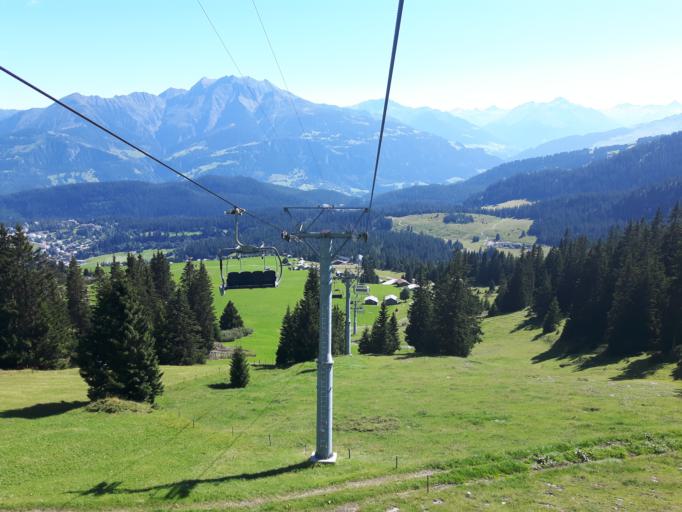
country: CH
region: Grisons
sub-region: Imboden District
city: Flims
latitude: 46.8547
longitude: 9.2683
